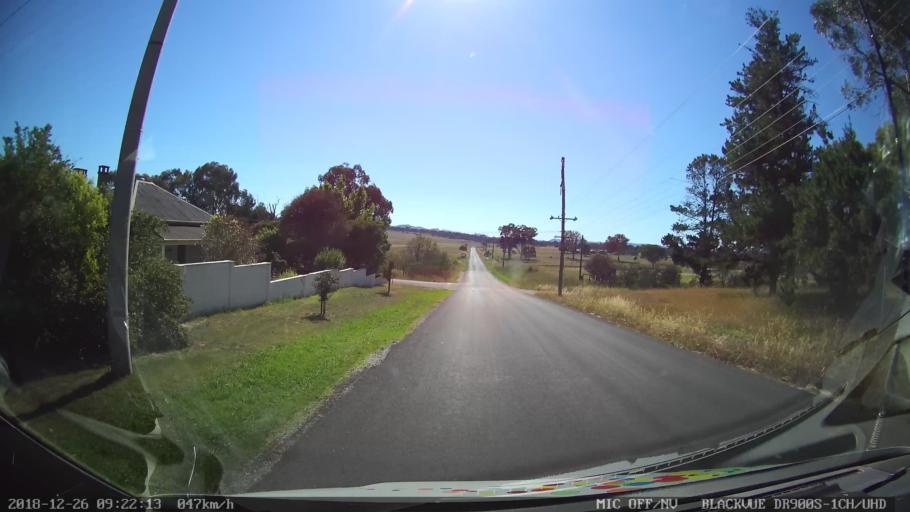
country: AU
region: New South Wales
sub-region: Mid-Western Regional
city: Kandos
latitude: -32.8036
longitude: 149.9759
